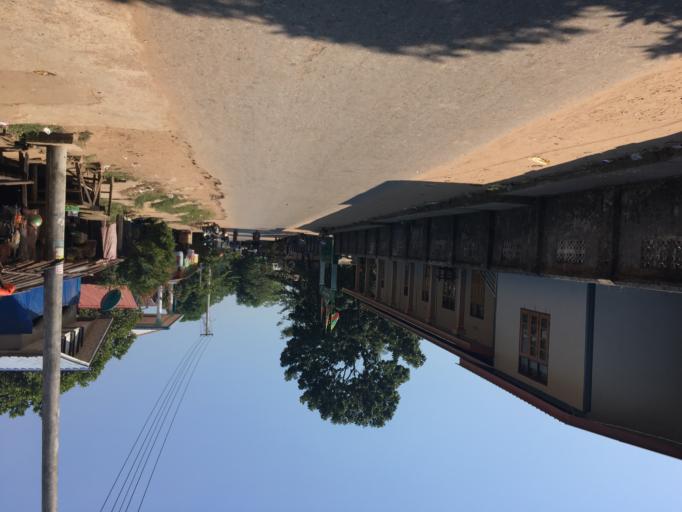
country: MM
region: Mon
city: Mawlamyine
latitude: 16.4349
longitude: 97.7032
